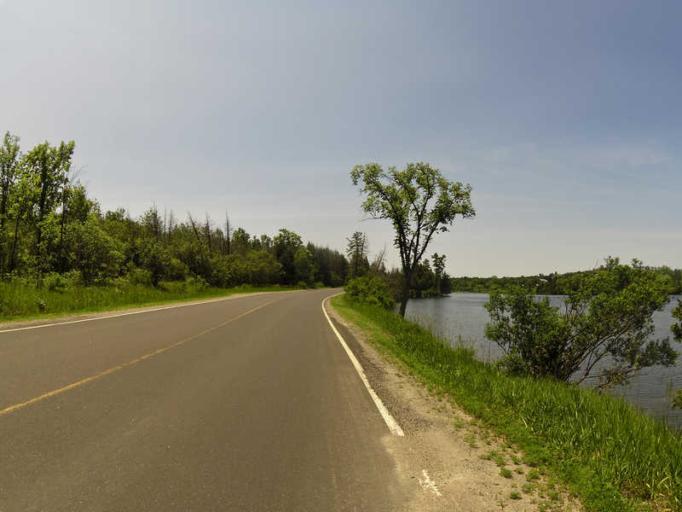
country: CA
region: Ontario
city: Peterborough
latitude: 44.3795
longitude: -78.2805
